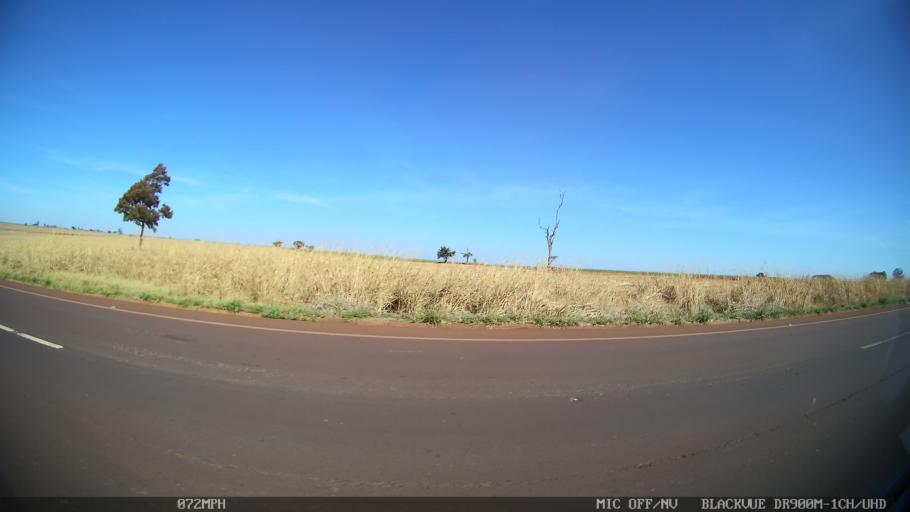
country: BR
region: Sao Paulo
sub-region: Ipua
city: Ipua
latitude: -20.4790
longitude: -48.0840
